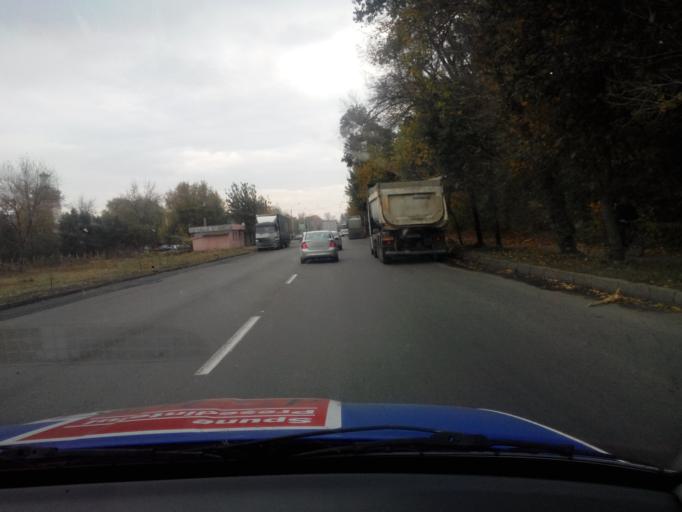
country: RO
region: Vaslui
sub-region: Municipiul Barlad
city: Barlad
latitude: 46.2528
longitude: 27.6830
